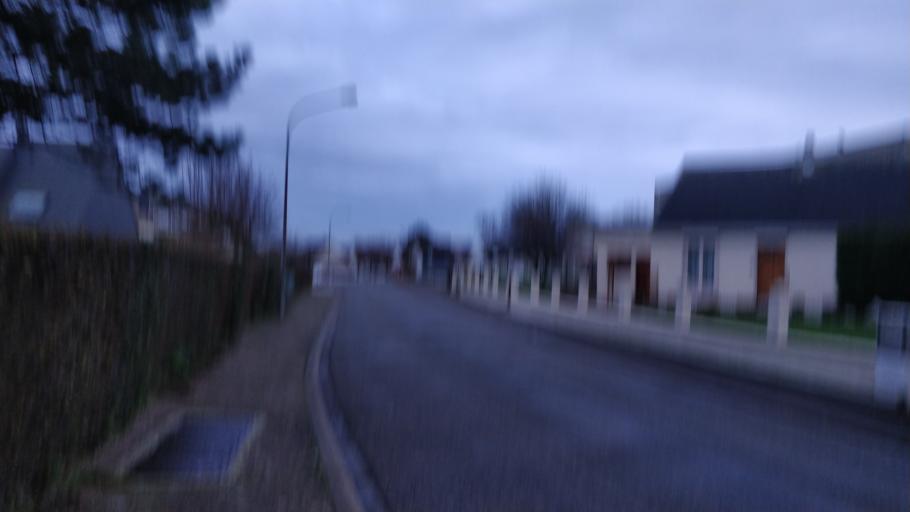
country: FR
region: Haute-Normandie
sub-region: Departement de la Seine-Maritime
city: Le Treport
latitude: 50.0570
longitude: 1.3654
